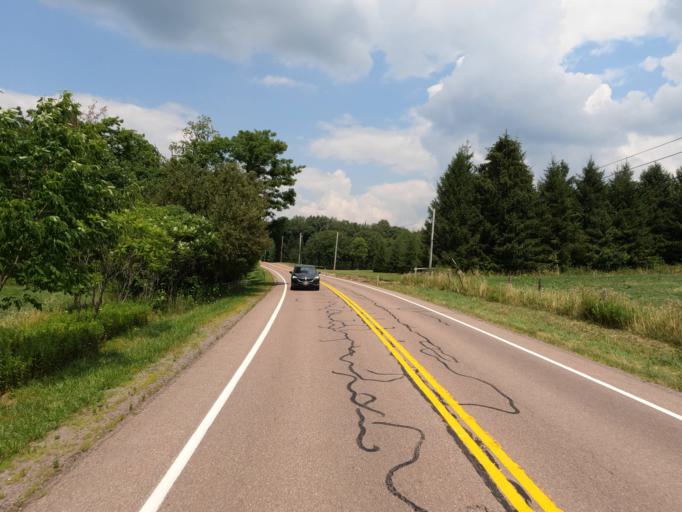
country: US
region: Maryland
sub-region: Allegany County
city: Westernport
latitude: 39.6398
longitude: -79.2030
